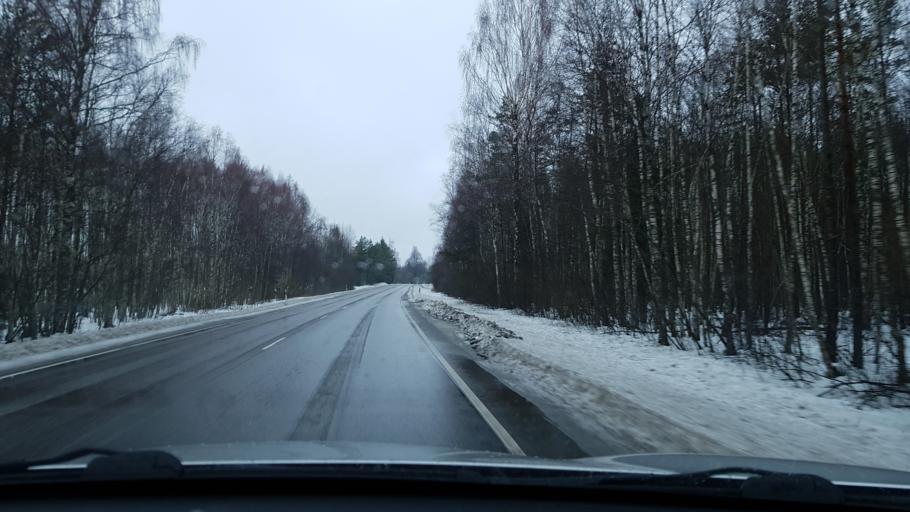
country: EE
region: Raplamaa
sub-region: Kehtna vald
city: Kehtna
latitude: 58.8672
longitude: 24.9889
